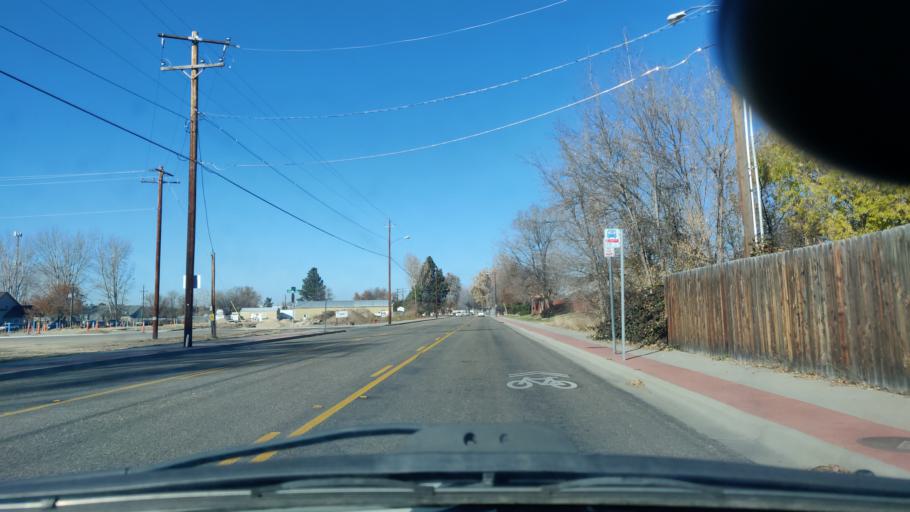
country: US
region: Idaho
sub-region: Ada County
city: Garden City
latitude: 43.6427
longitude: -116.2587
